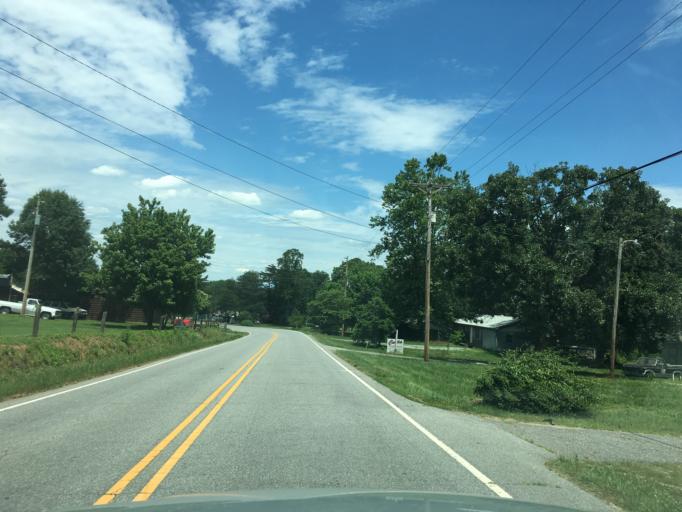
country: US
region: North Carolina
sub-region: Burke County
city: Glen Alpine
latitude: 35.6760
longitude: -81.7679
